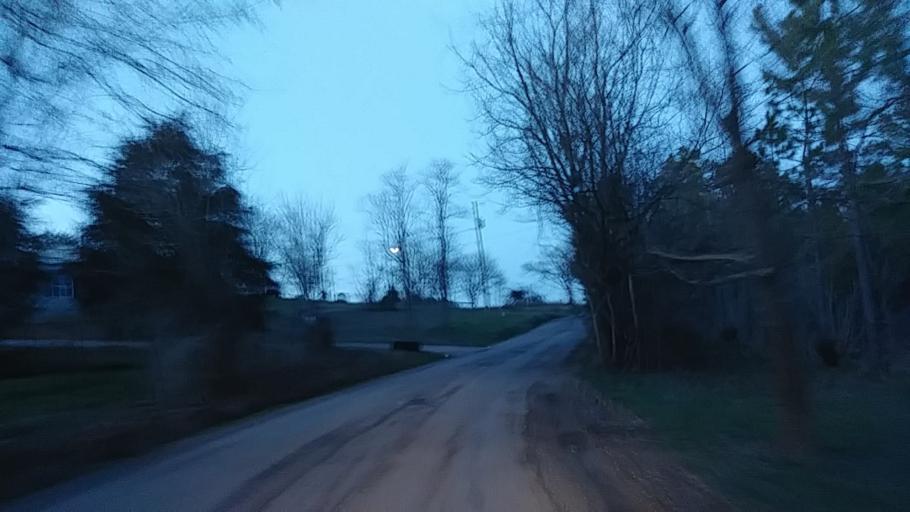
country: US
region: Tennessee
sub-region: Greene County
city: Mosheim
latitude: 36.0685
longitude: -82.9885
